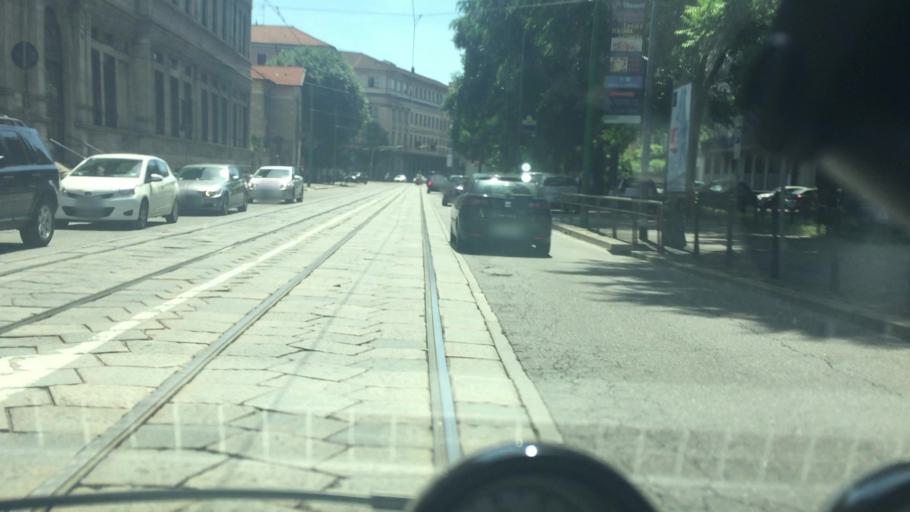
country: IT
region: Lombardy
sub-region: Citta metropolitana di Milano
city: Milano
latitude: 45.4887
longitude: 9.2223
